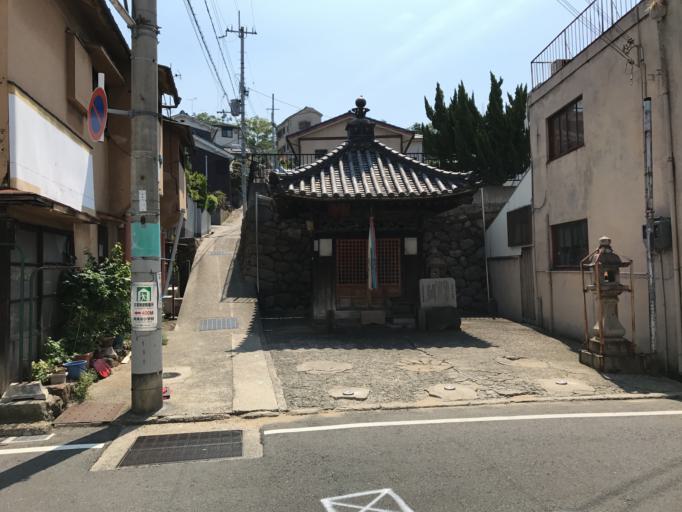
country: JP
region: Osaka
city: Kashihara
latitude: 34.6067
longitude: 135.6321
